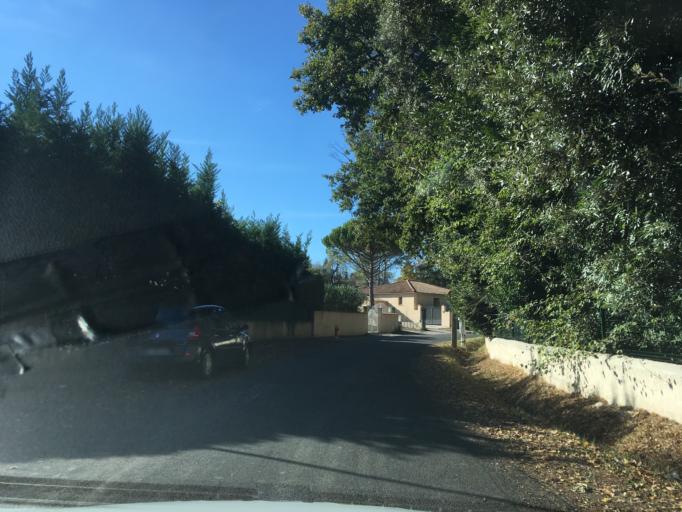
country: FR
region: Languedoc-Roussillon
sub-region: Departement de l'Herault
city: Saint-Jean-de-Vedas
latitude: 43.5966
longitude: 3.8320
